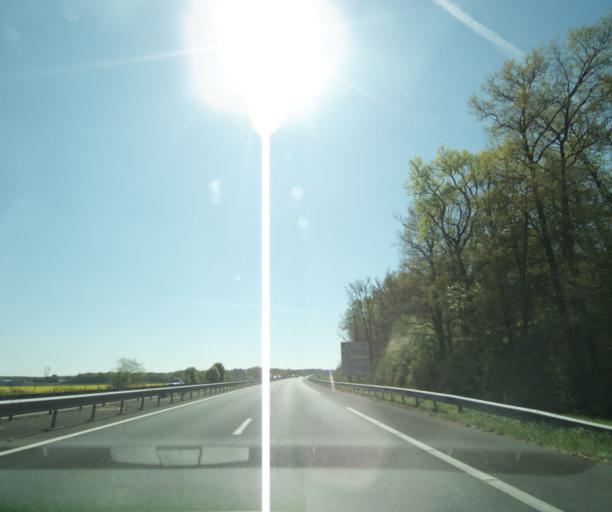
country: FR
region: Centre
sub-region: Departement de l'Indre
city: Saint-Maur
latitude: 46.7813
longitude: 1.6309
